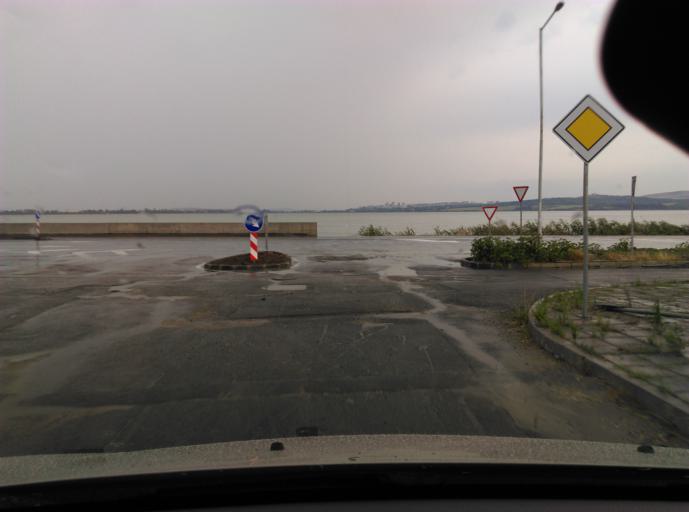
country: BG
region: Burgas
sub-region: Obshtina Burgas
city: Burgas
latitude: 42.5120
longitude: 27.4305
